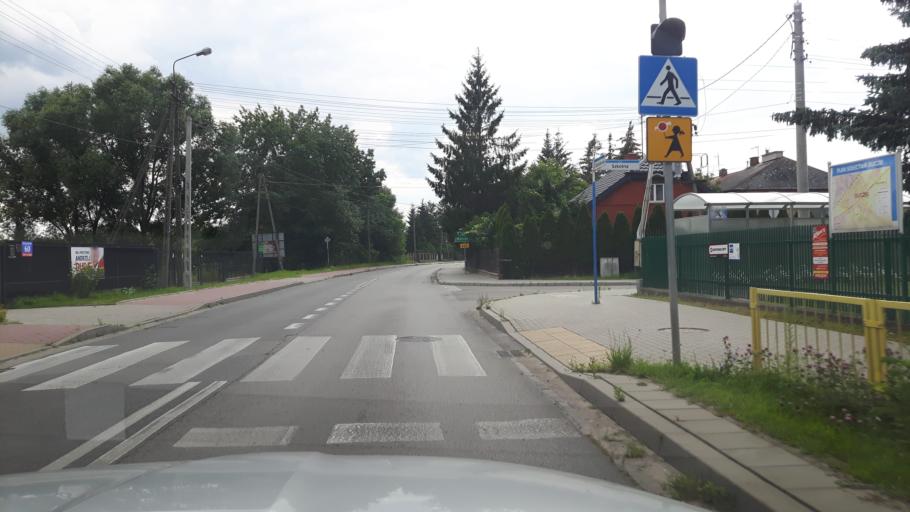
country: PL
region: Masovian Voivodeship
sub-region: Powiat wolominski
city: Duczki
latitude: 52.3619
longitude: 21.2893
